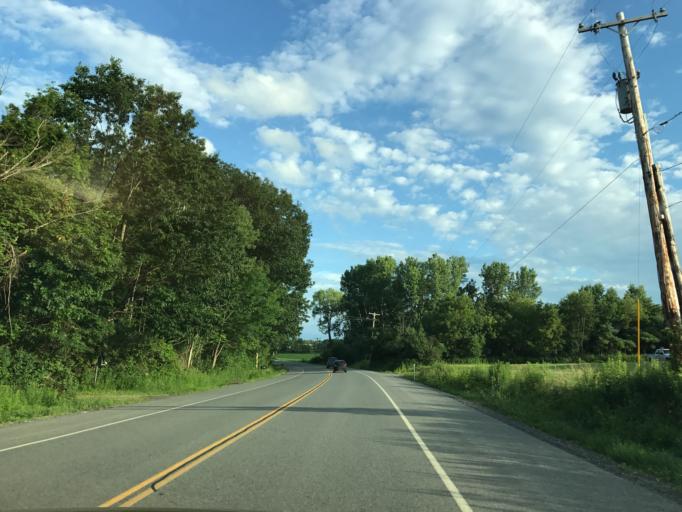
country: US
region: New York
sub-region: Saratoga County
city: Schuylerville
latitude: 43.0572
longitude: -73.5956
